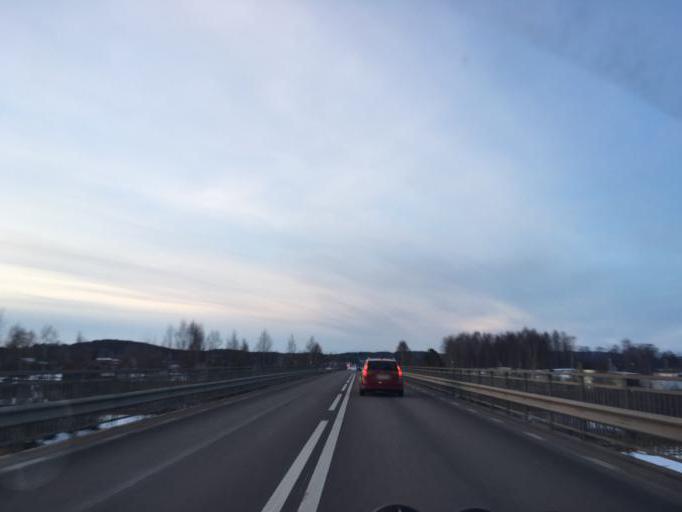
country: SE
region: Dalarna
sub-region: Leksand Municipality
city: Leksand
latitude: 60.7284
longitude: 15.0094
